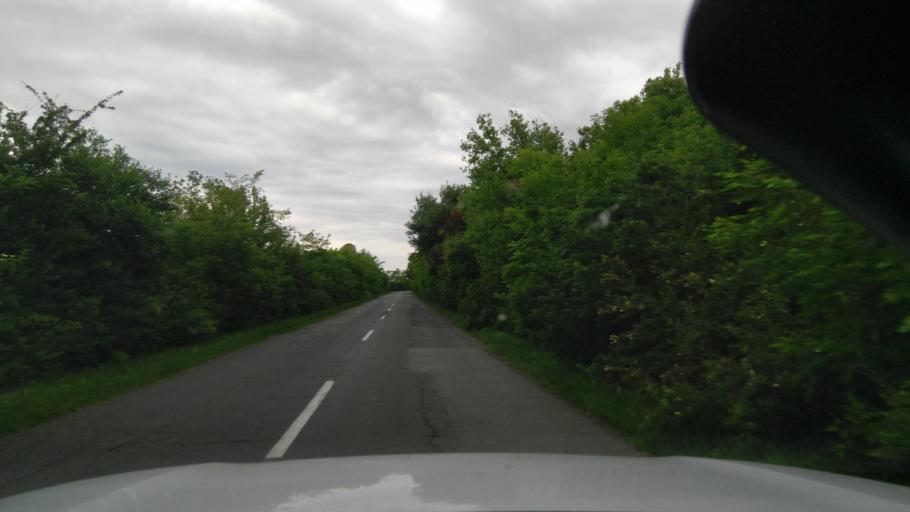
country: HU
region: Bekes
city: Bekescsaba
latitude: 46.6756
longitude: 21.1722
